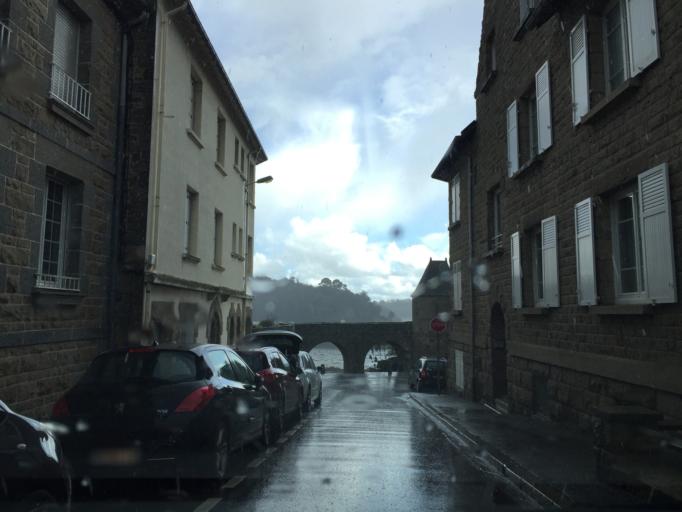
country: FR
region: Brittany
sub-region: Departement d'Ille-et-Vilaine
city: Saint-Malo
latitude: 48.6349
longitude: -2.0256
